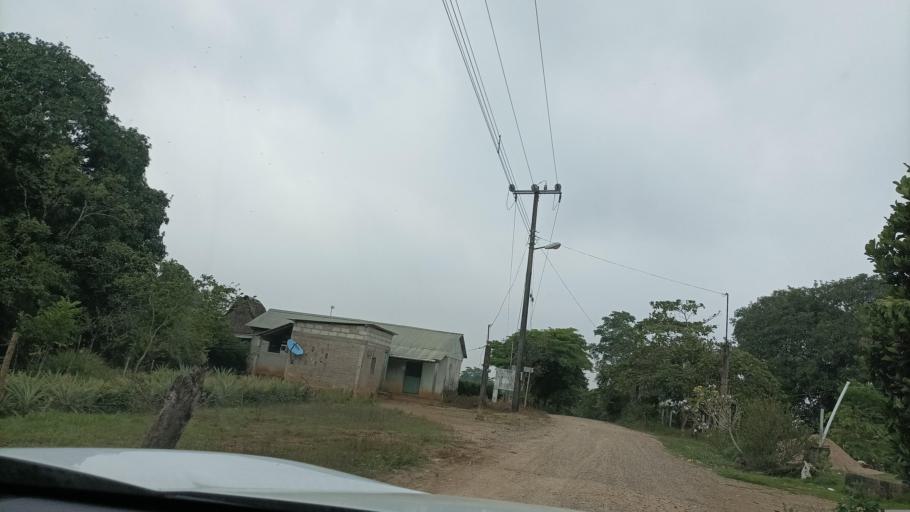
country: MX
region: Veracruz
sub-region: Uxpanapa
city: Poblado 10
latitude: 17.5538
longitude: -94.2250
